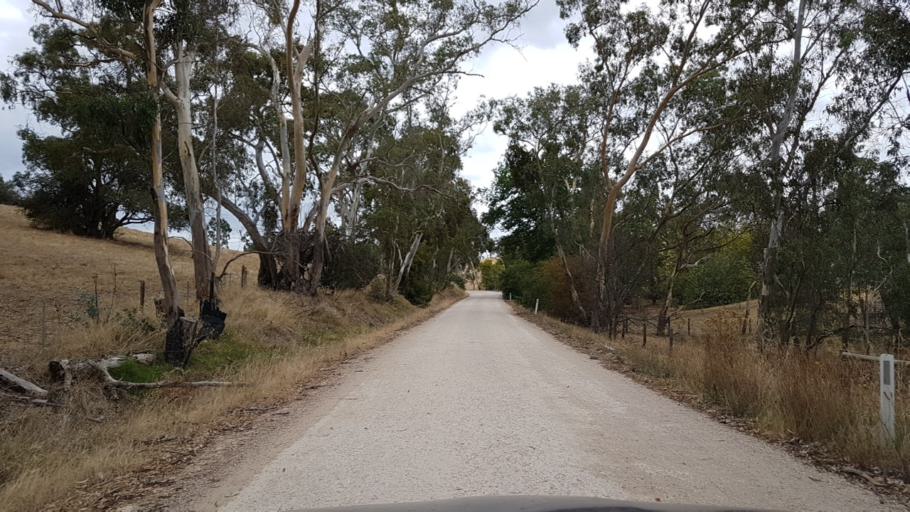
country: AU
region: South Australia
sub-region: Adelaide Hills
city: Gumeracha
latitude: -34.8063
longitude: 138.8099
